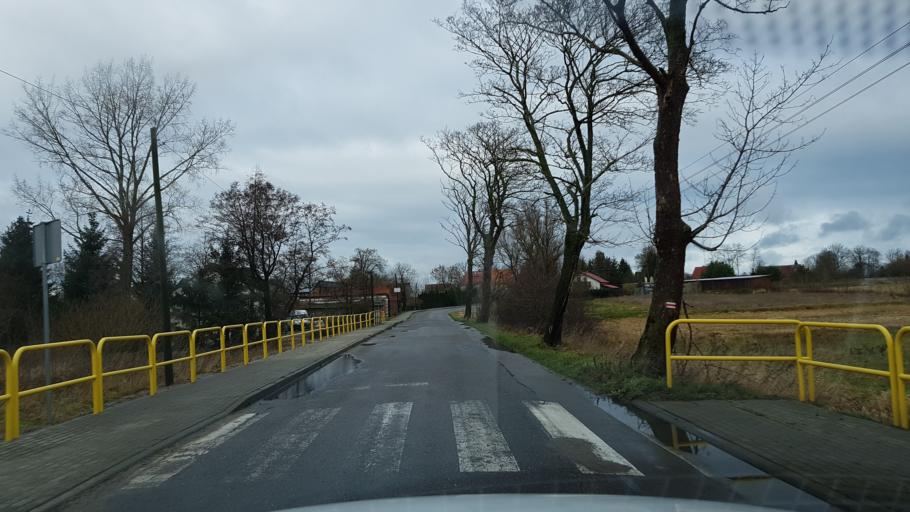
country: PL
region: West Pomeranian Voivodeship
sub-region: Powiat slawienski
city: Slawno
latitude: 54.5111
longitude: 16.6544
